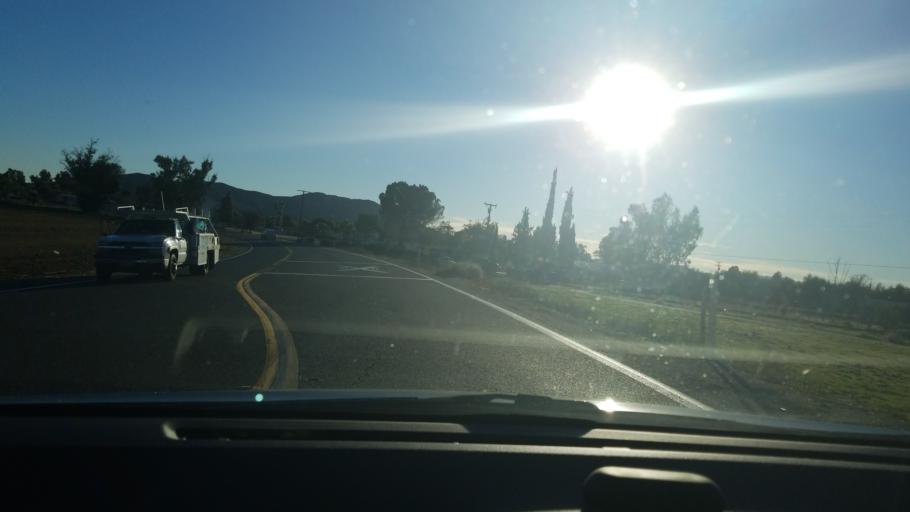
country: US
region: California
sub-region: Riverside County
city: Winchester
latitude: 33.7126
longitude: -117.0844
